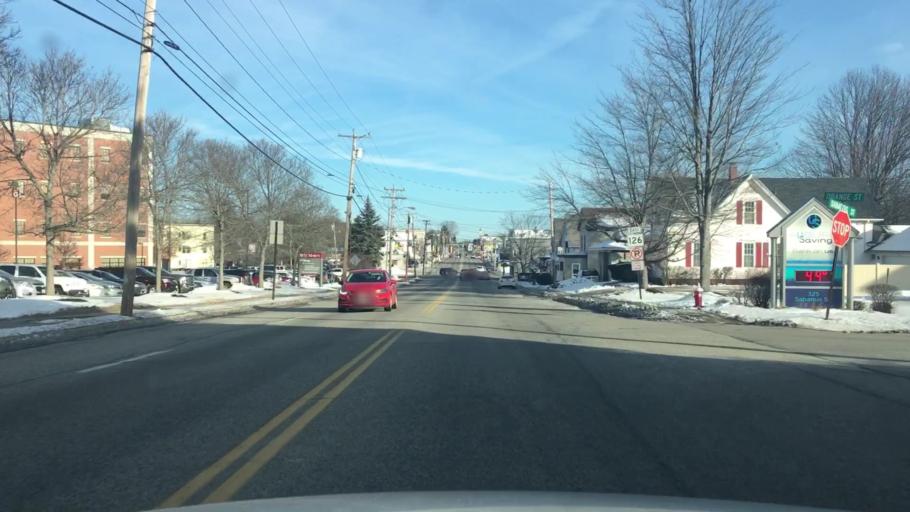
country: US
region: Maine
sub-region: Androscoggin County
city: Lewiston
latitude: 44.1007
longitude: -70.1995
